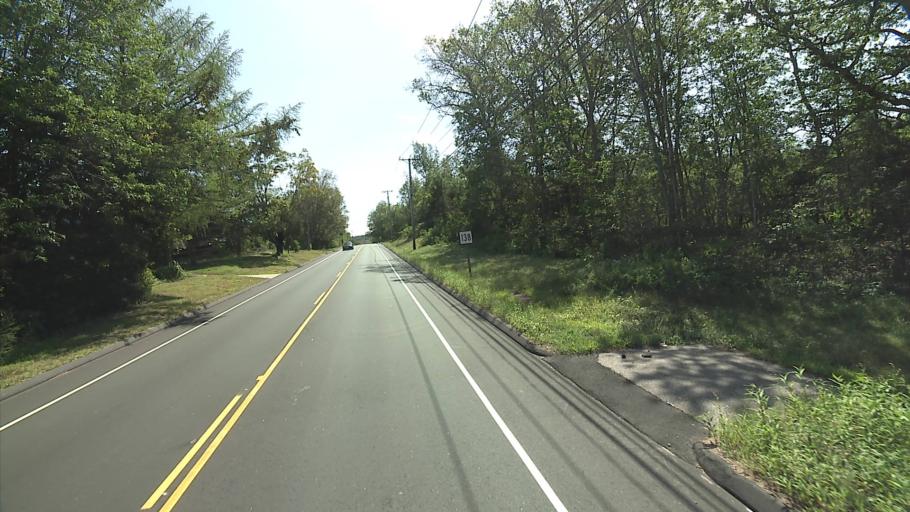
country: US
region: Connecticut
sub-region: New London County
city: Preston City
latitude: 41.5754
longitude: -71.8835
